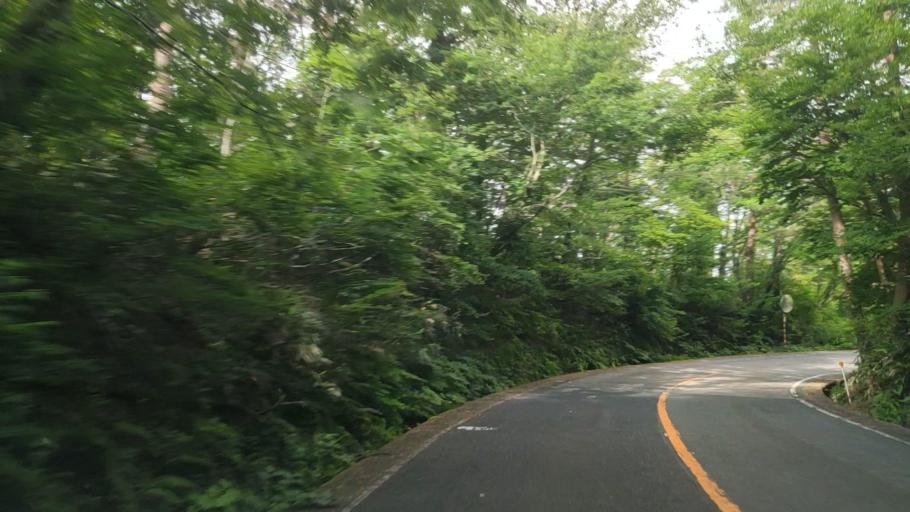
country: JP
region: Tottori
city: Yonago
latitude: 35.3669
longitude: 133.5168
